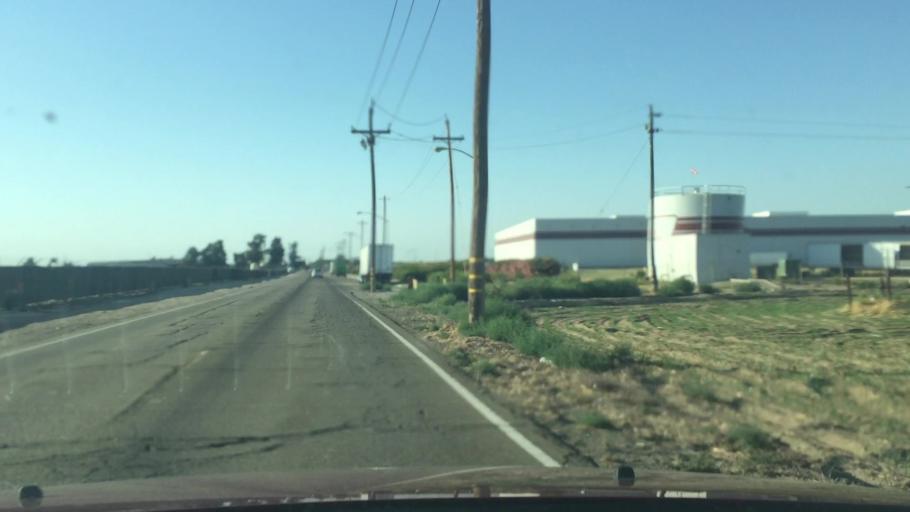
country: US
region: California
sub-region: San Joaquin County
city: Lathrop
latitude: 37.8041
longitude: -121.2709
